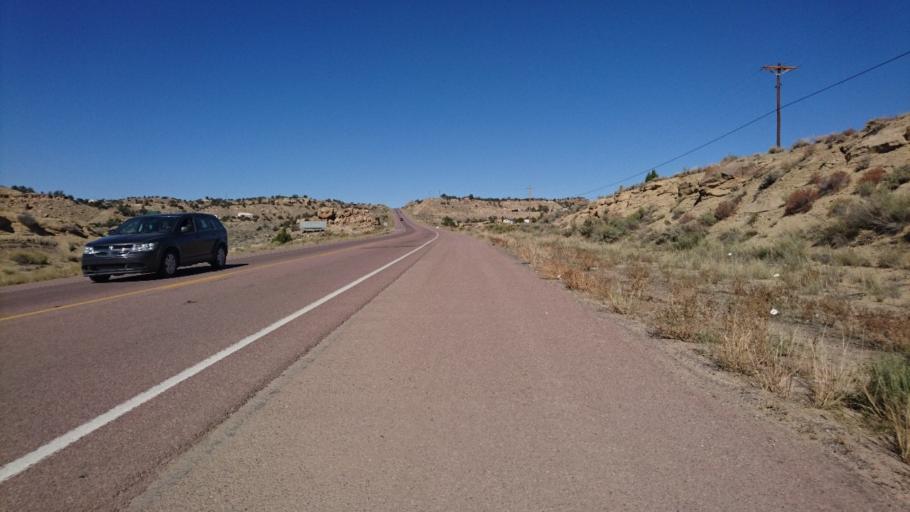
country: US
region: New Mexico
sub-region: McKinley County
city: Gallup
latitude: 35.4677
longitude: -108.7426
